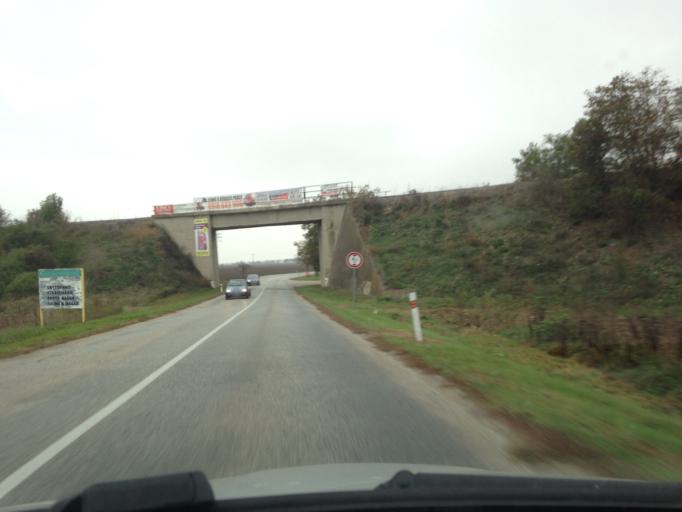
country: SK
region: Nitriansky
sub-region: Okres Nove Zamky
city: Sturovo
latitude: 47.8003
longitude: 18.6605
